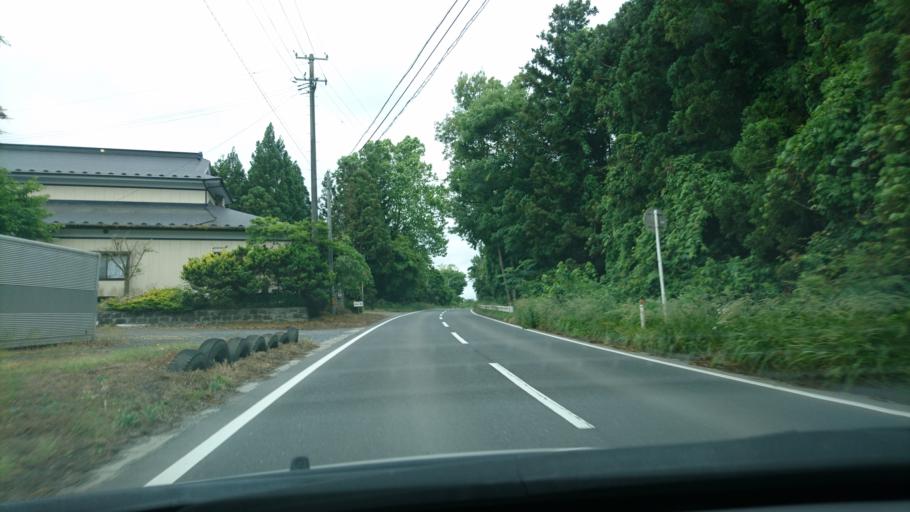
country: JP
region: Iwate
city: Ichinoseki
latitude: 38.7567
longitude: 141.2562
